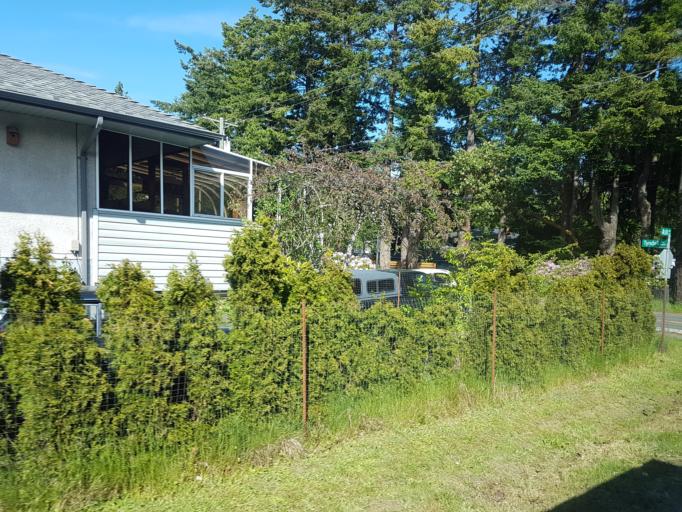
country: CA
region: British Columbia
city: Oak Bay
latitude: 48.4896
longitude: -123.3181
